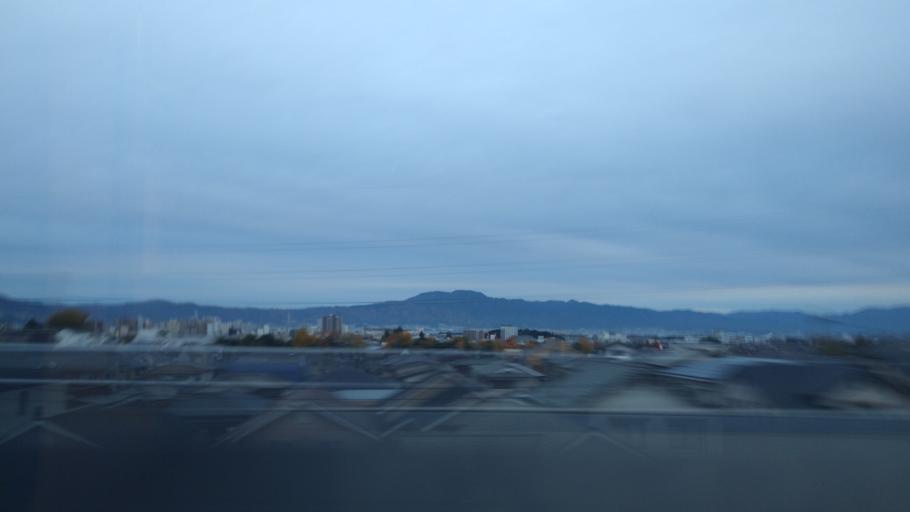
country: JP
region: Shiga Prefecture
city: Kusatsu
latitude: 34.9804
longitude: 135.9393
